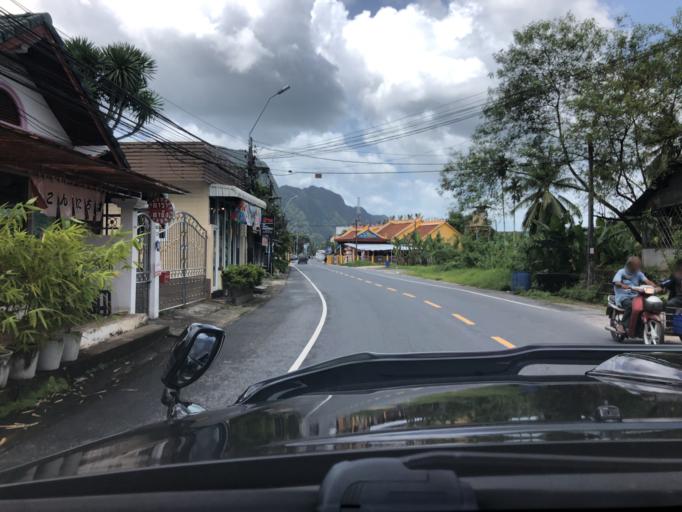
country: TH
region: Phangnga
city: Phang Nga
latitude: 8.4675
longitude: 98.5321
